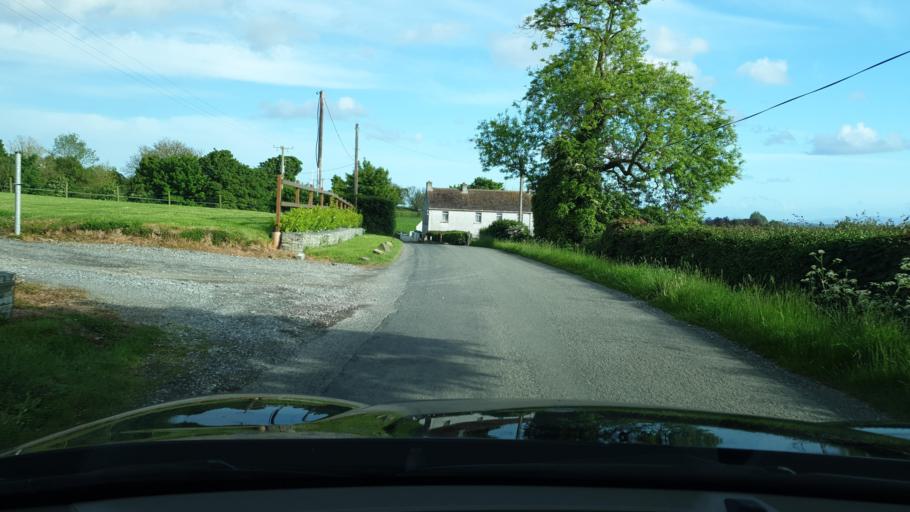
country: IE
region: Leinster
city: Balrothery
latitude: 53.5494
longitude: -6.2054
